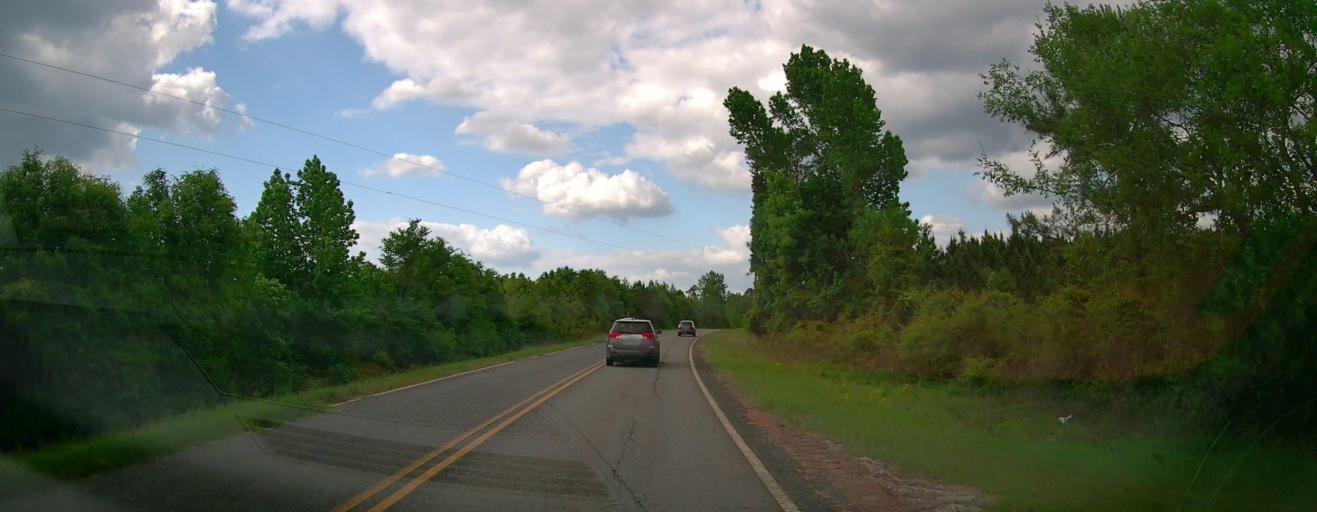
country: US
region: Georgia
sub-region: Washington County
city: Tennille
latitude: 32.7641
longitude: -82.9306
